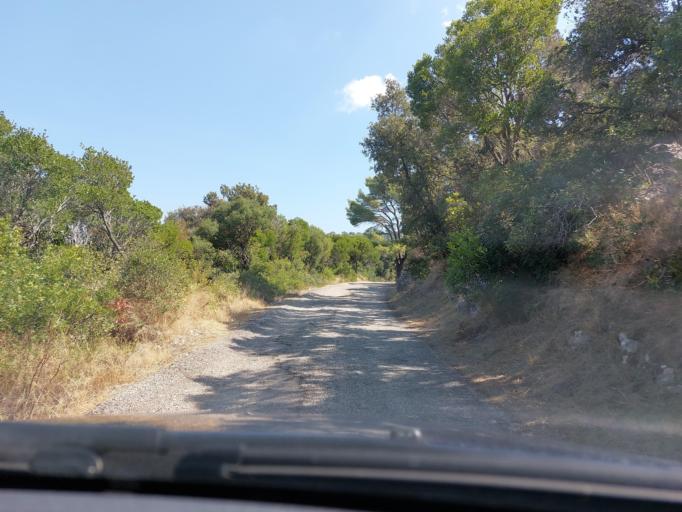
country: HR
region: Dubrovacko-Neretvanska
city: Smokvica
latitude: 42.7674
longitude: 16.8276
